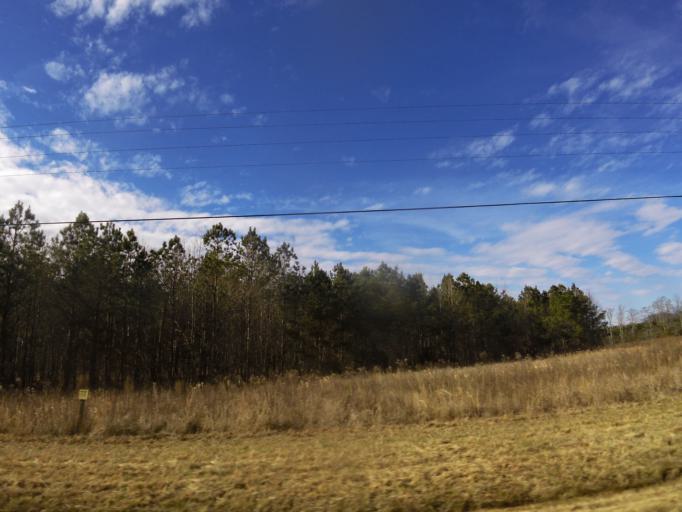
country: US
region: Virginia
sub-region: City of Franklin
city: Franklin
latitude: 36.7091
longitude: -76.8831
